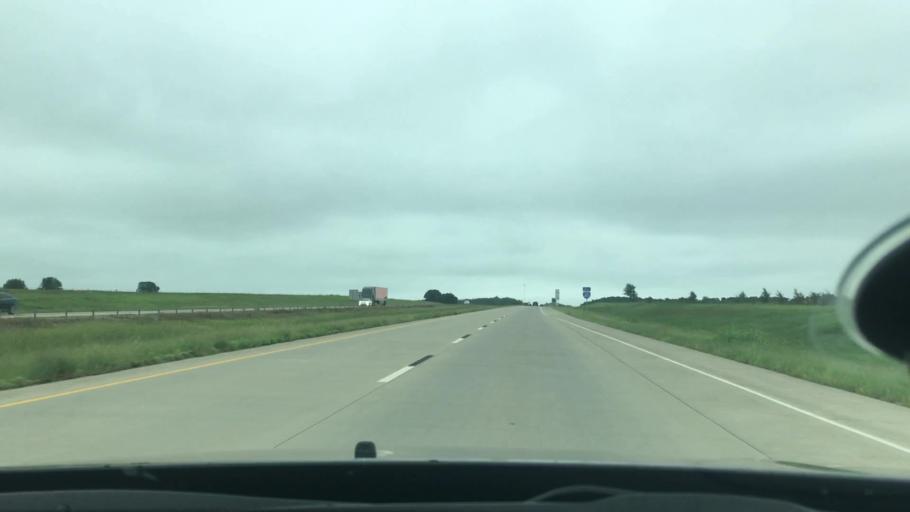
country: US
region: Oklahoma
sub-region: McIntosh County
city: Checotah
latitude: 35.4571
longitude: -95.4464
